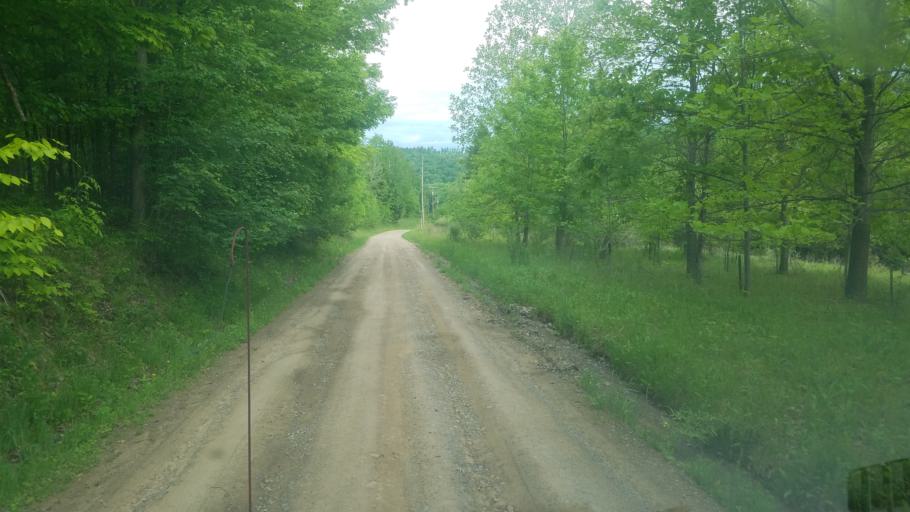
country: US
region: Pennsylvania
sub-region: Tioga County
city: Westfield
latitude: 41.9298
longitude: -77.6950
